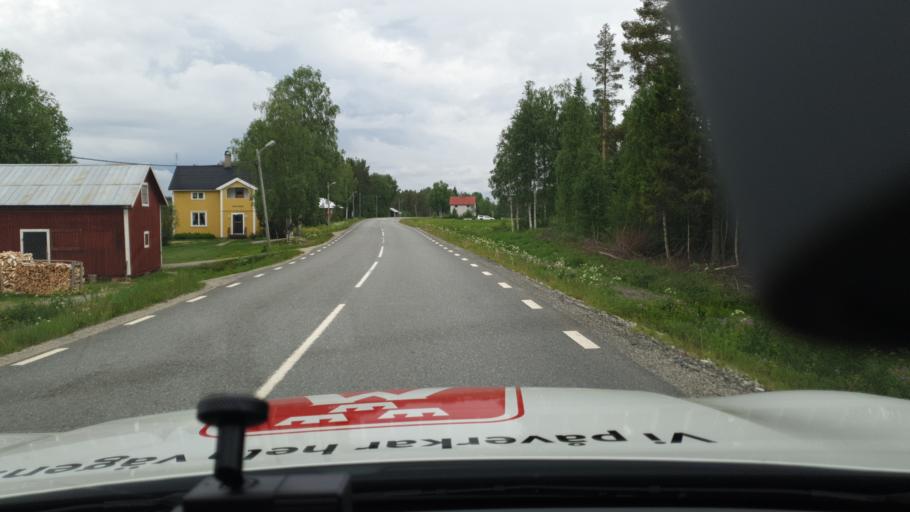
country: SE
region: Vaesterbotten
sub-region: Bjurholms Kommun
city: Bjurholm
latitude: 64.3563
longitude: 19.1424
